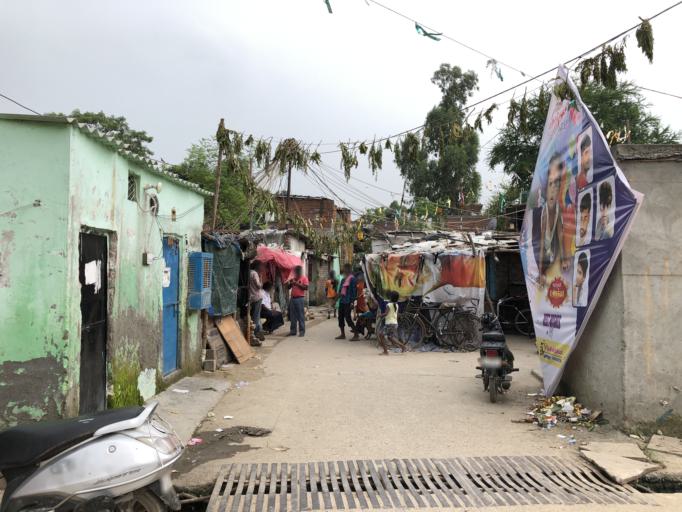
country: IN
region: NCT
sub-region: New Delhi
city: New Delhi
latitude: 28.5785
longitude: 77.2501
